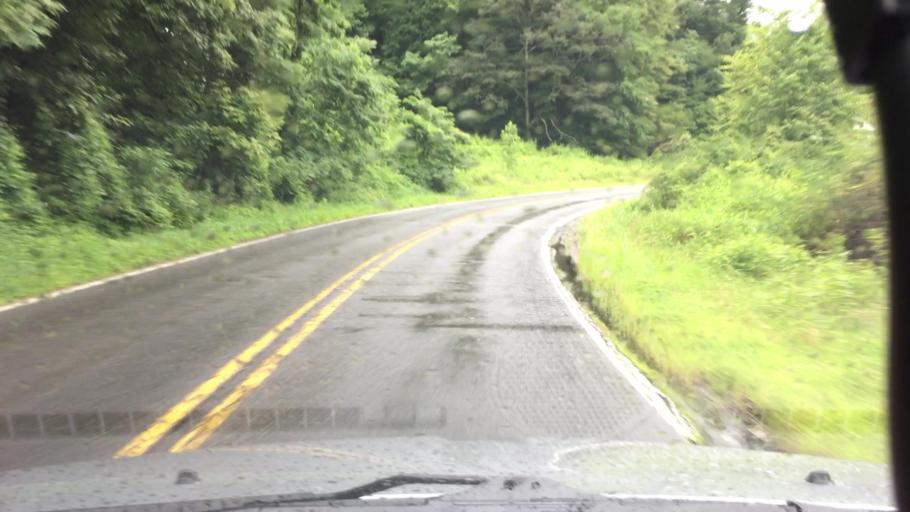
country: US
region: North Carolina
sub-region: Madison County
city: Mars Hill
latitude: 35.9261
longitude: -82.5324
